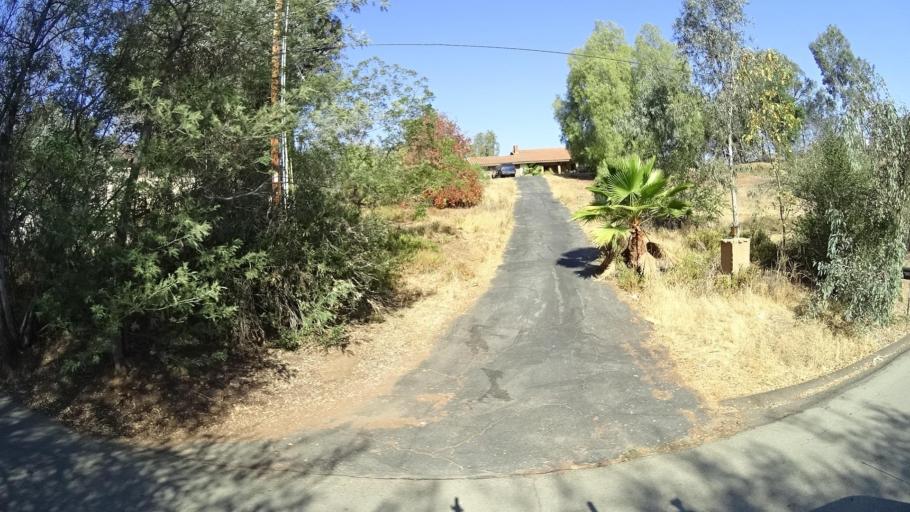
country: US
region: California
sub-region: San Diego County
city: Fallbrook
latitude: 33.3978
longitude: -117.2263
